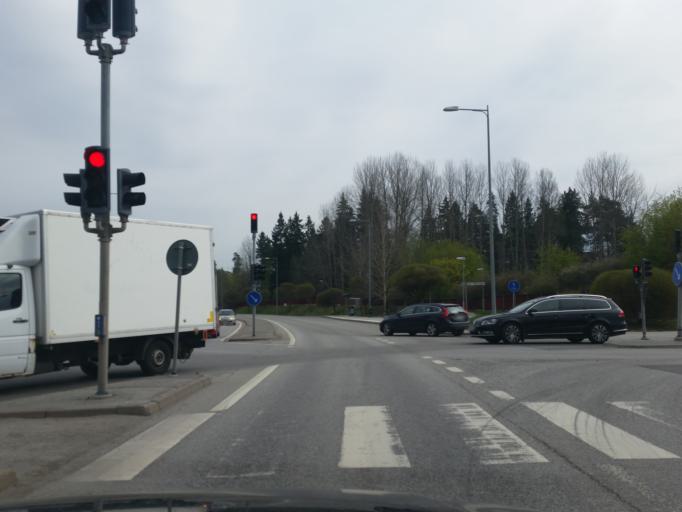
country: SE
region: Stockholm
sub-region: Taby Kommun
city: Taby
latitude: 59.4678
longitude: 18.0544
